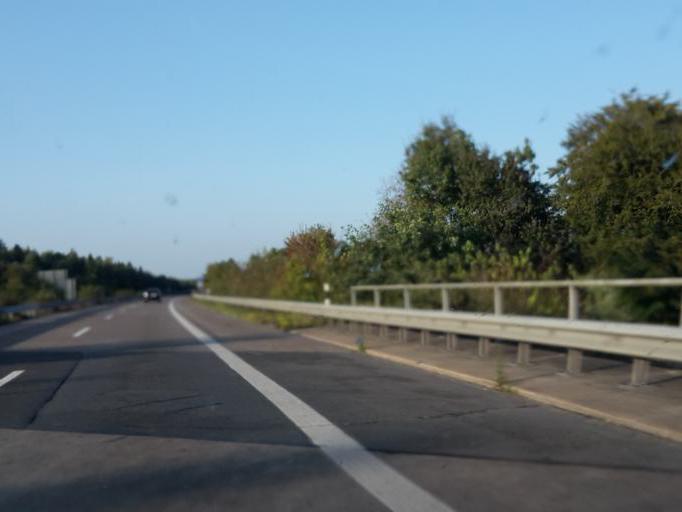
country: DE
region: Lower Saxony
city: Emstek
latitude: 52.9038
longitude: 8.1646
